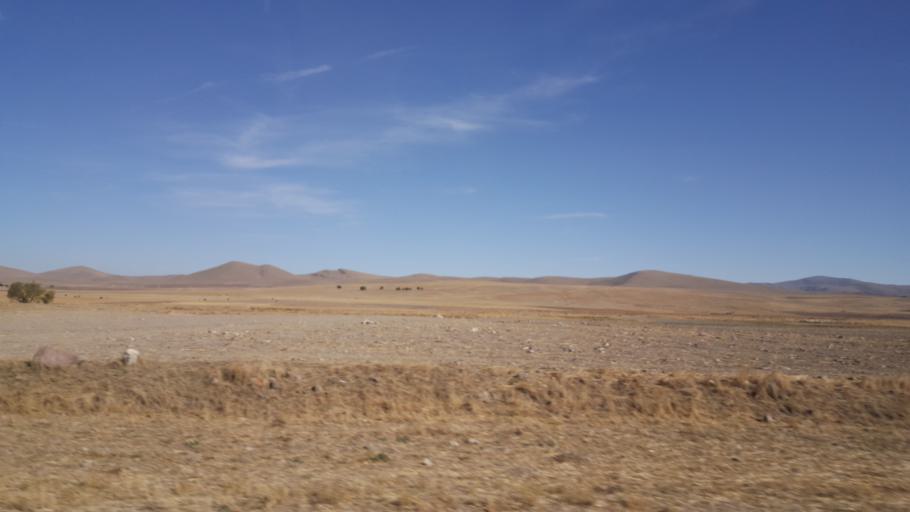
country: TR
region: Ankara
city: Altpinar
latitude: 39.2544
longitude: 32.7524
